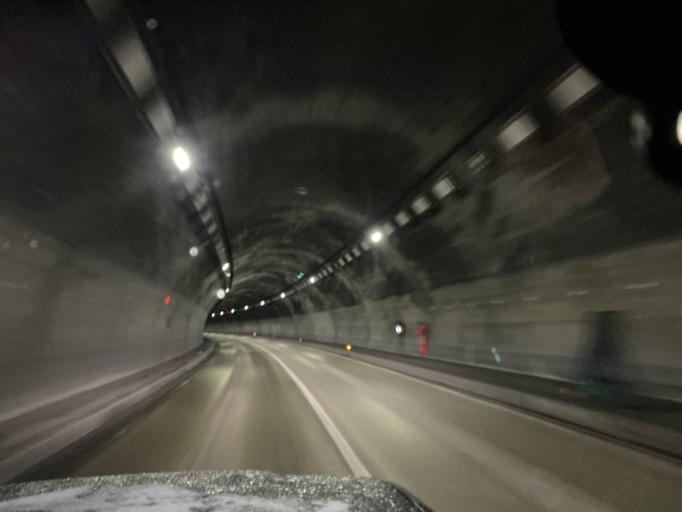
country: JP
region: Nagano
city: Omachi
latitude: 36.5431
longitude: 137.8443
